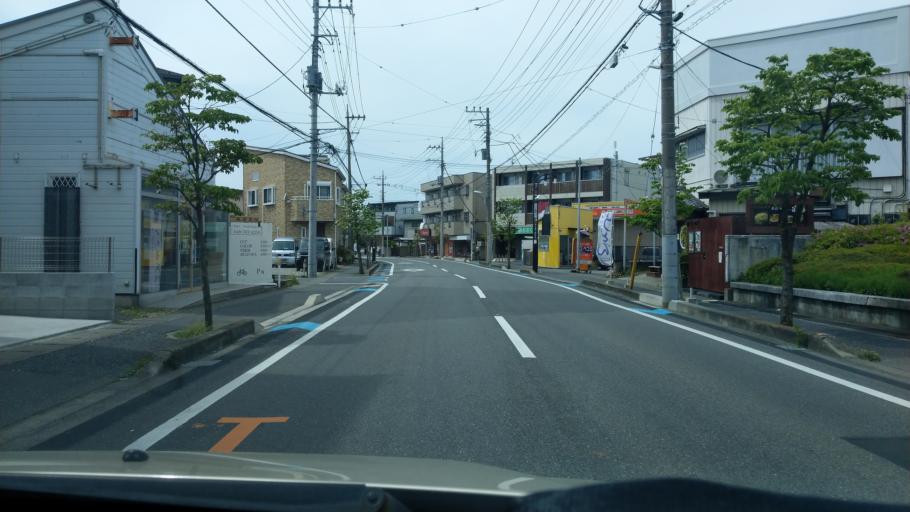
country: JP
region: Saitama
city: Yono
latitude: 35.8679
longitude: 139.6126
